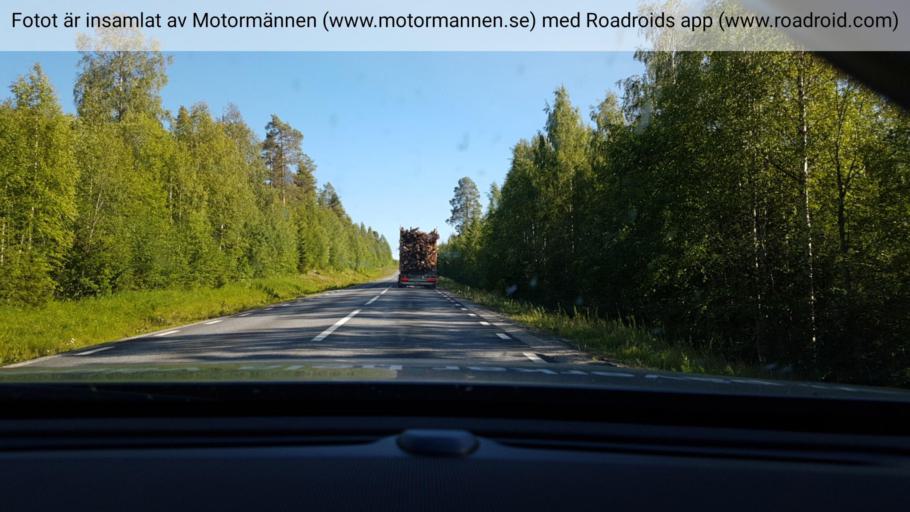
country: SE
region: Vaesterbotten
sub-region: Bjurholms Kommun
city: Bjurholm
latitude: 64.3301
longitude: 19.1530
